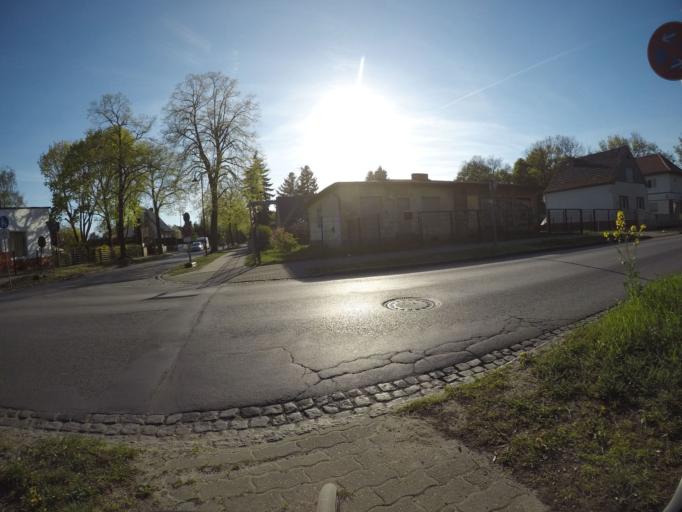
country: DE
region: Brandenburg
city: Neuenhagen
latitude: 52.5193
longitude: 13.7067
